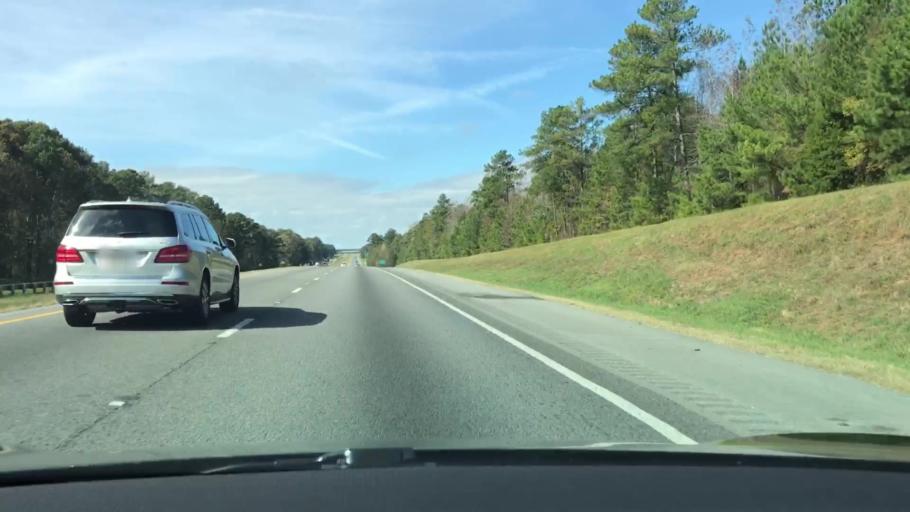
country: US
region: Georgia
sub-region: Walton County
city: Social Circle
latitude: 33.6046
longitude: -83.6702
